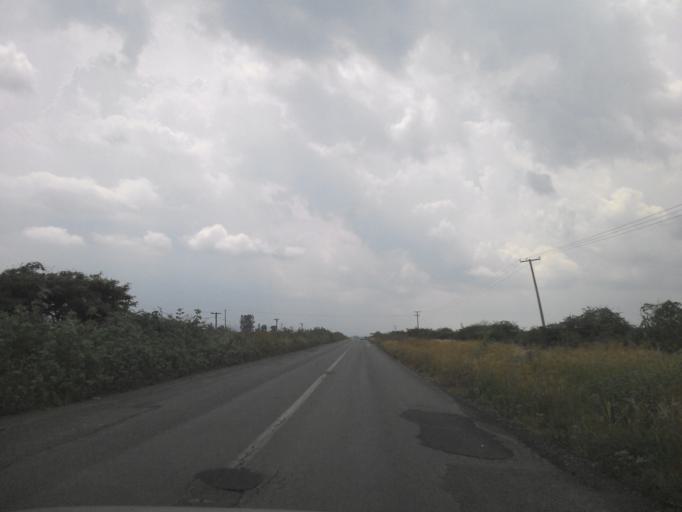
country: MX
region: Guanajuato
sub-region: San Francisco del Rincon
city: San Ignacio de Hidalgo
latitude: 20.8916
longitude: -101.9427
